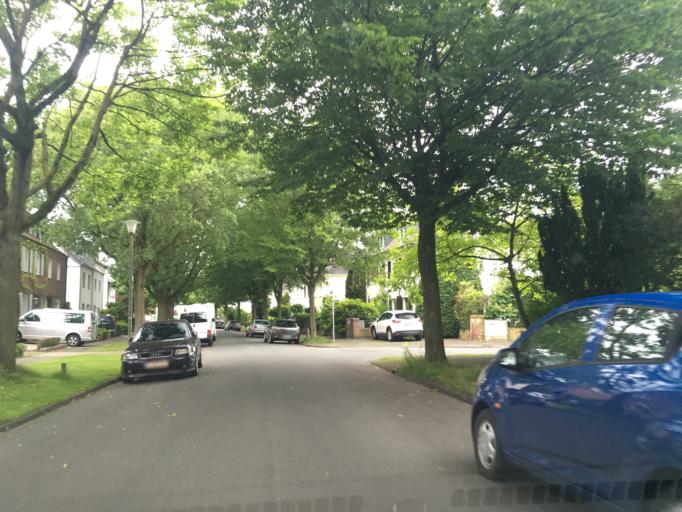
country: DE
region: North Rhine-Westphalia
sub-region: Regierungsbezirk Munster
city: Muenster
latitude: 51.9368
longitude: 7.6187
